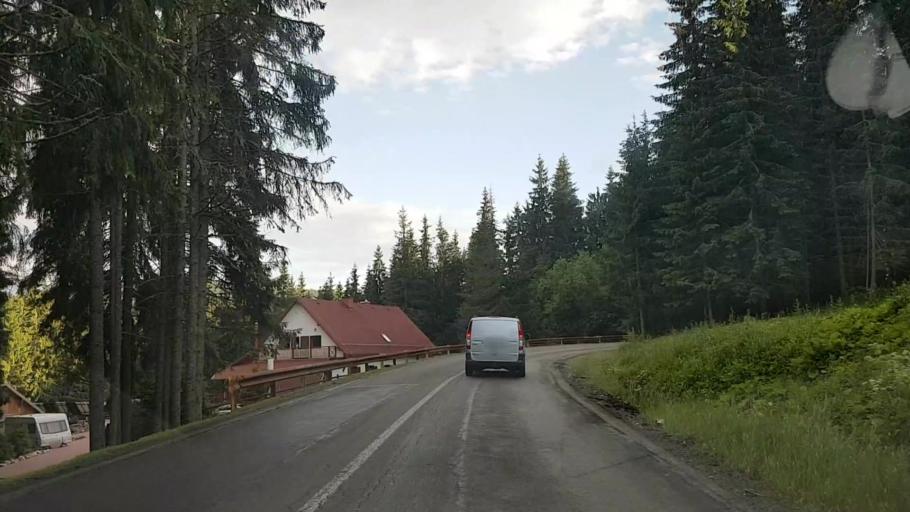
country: RO
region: Harghita
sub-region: Comuna Varsag
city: Varsag
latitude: 46.6624
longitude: 25.3042
